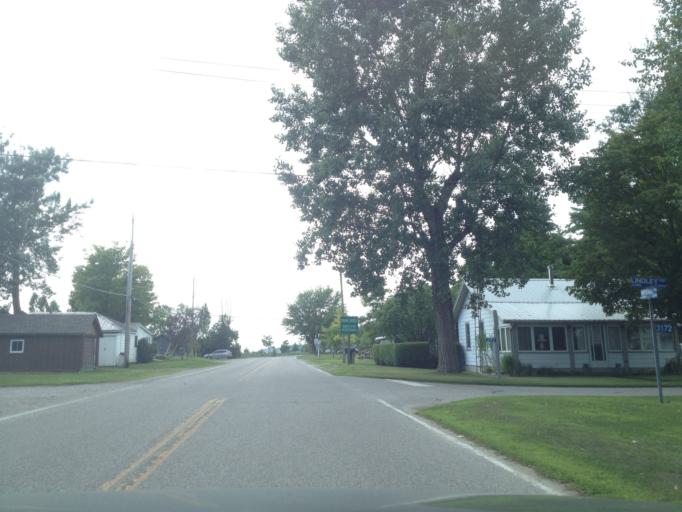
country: CA
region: Ontario
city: Aylmer
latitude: 42.6546
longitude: -81.0098
